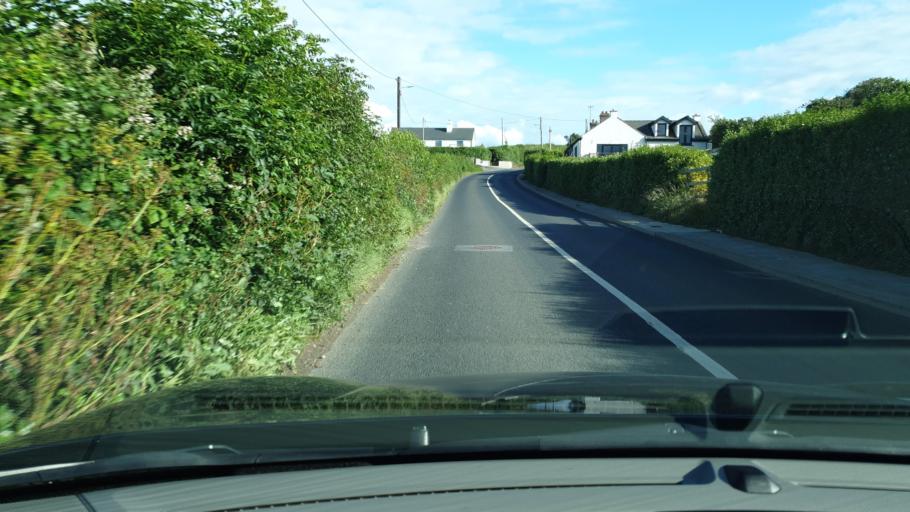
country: IE
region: Leinster
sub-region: Fingal County
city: Skerries
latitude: 53.5576
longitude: -6.1020
